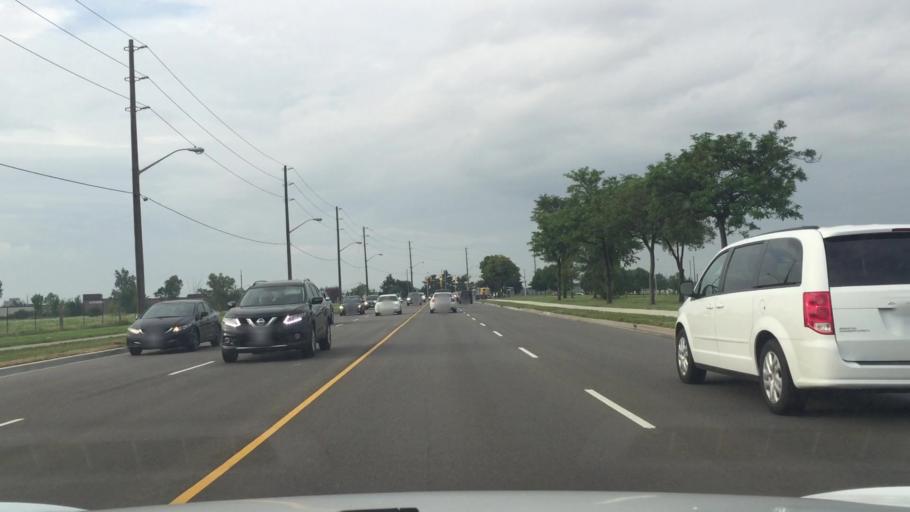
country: CA
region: Ontario
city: Concord
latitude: 43.7506
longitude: -79.4828
